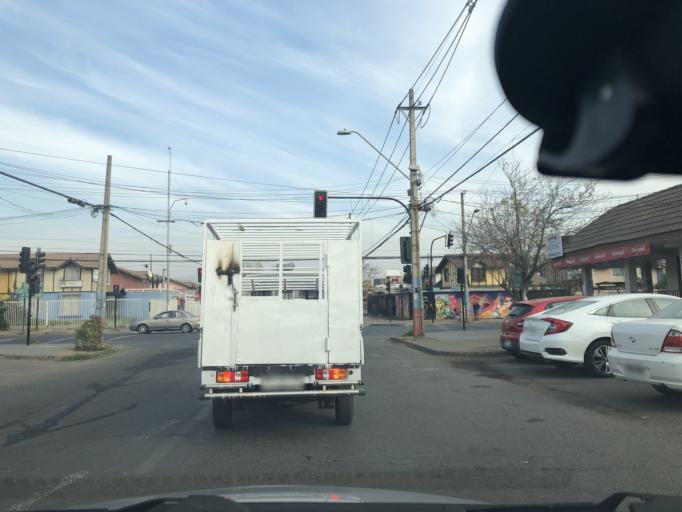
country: CL
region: Santiago Metropolitan
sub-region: Provincia de Cordillera
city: Puente Alto
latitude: -33.5855
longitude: -70.5677
